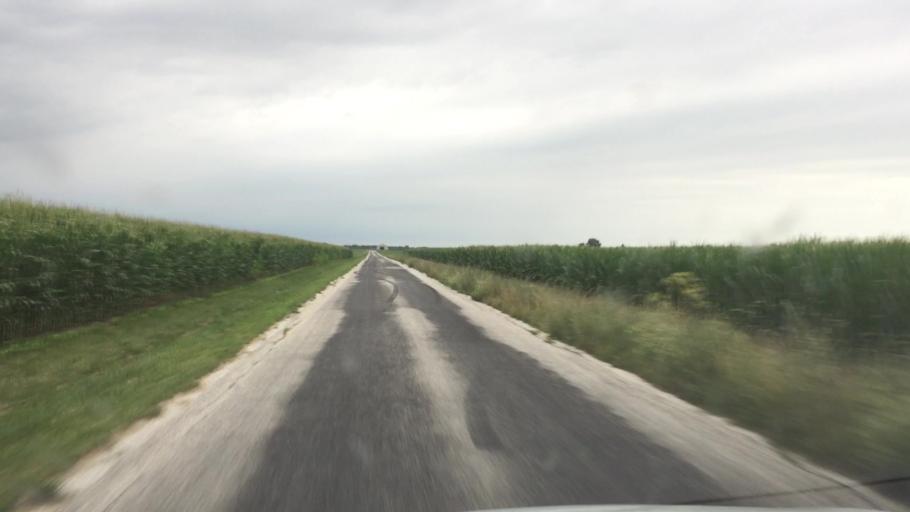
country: US
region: Illinois
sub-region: Adams County
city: Camp Point
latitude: 40.2208
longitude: -90.9691
